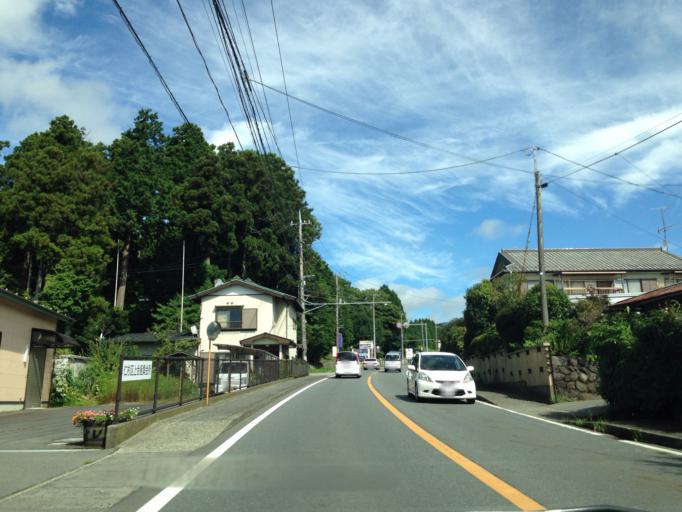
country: JP
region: Shizuoka
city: Gotemba
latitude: 35.3247
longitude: 138.9085
